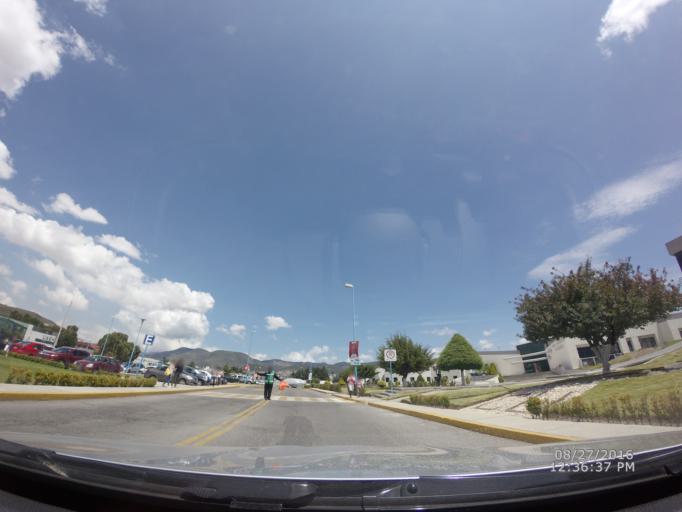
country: MX
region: Hidalgo
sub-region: Mineral de la Reforma
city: Carboneras
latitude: 20.0937
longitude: -98.7095
